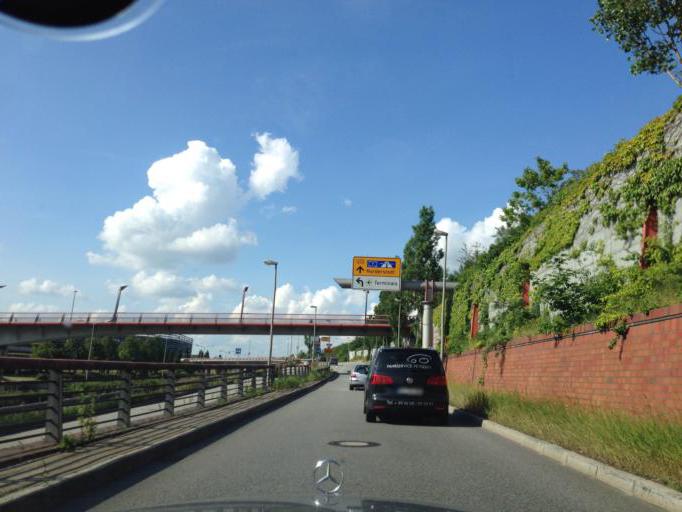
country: DE
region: Hamburg
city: Fuhlsbuettel
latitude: 53.6325
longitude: 10.0097
